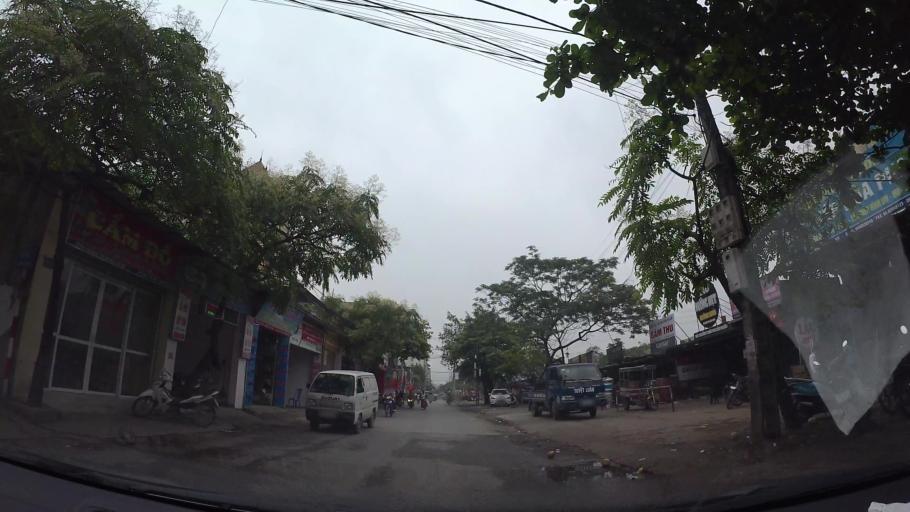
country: VN
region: Ha Noi
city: Hai BaTrung
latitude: 20.9851
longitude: 105.8716
